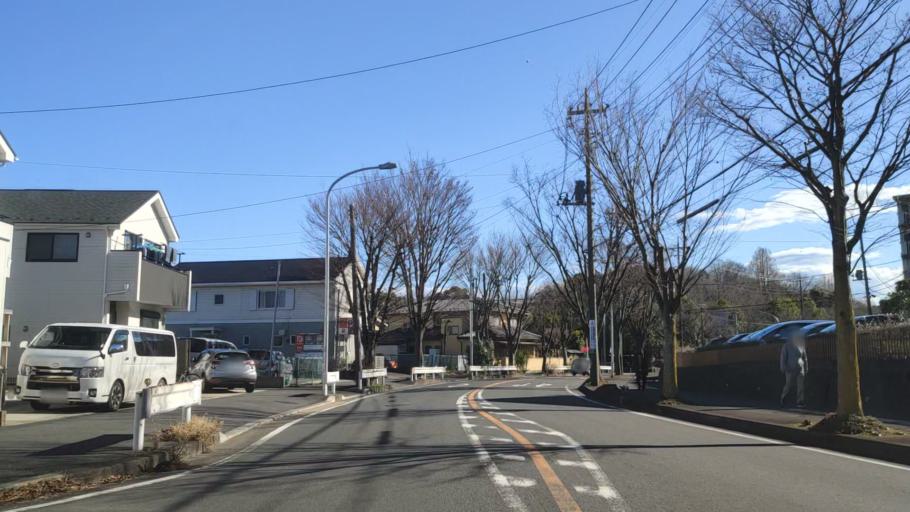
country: JP
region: Tokyo
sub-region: Machida-shi
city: Machida
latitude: 35.5153
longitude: 139.5001
